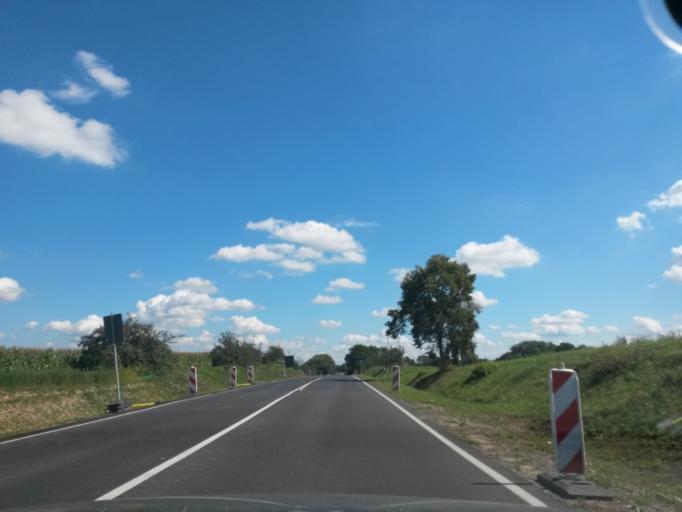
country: DE
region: Brandenburg
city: Pinnow
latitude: 53.0303
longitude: 14.0833
